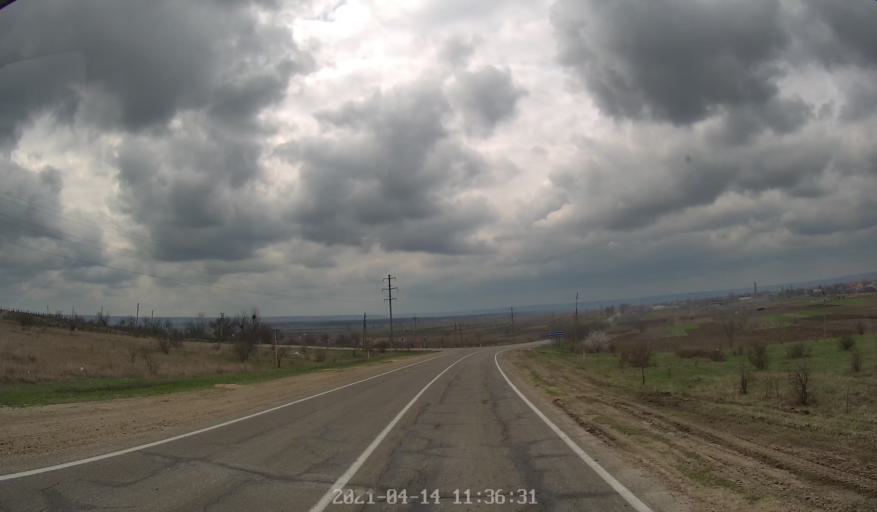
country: MD
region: Criuleni
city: Criuleni
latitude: 47.1600
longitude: 29.1629
